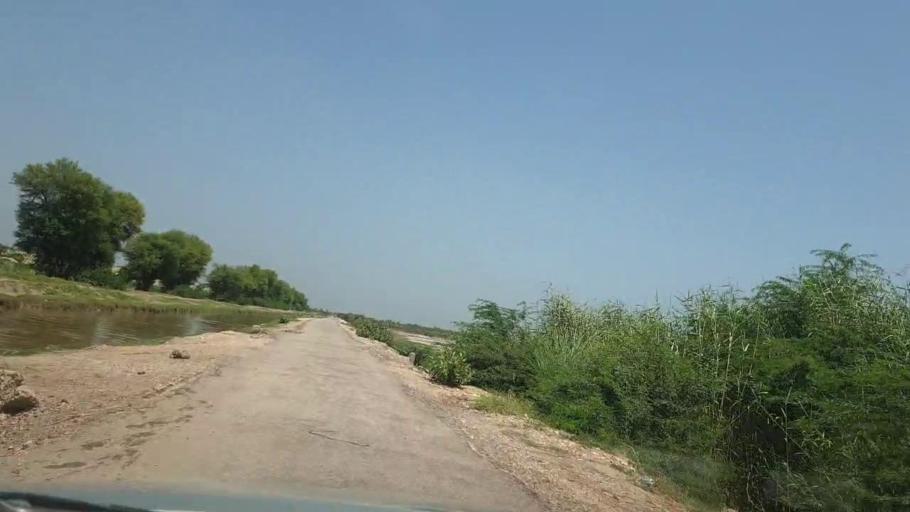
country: PK
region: Sindh
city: Rohri
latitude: 27.6168
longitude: 69.0991
